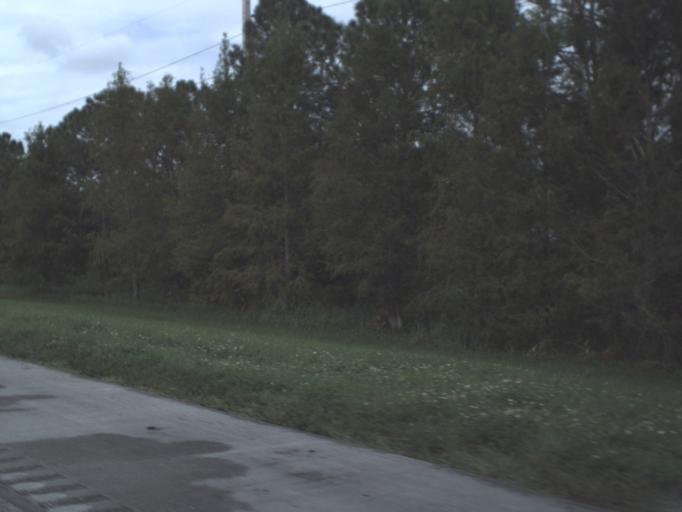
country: US
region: Florida
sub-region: Martin County
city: Palm City
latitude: 27.1783
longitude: -80.3159
